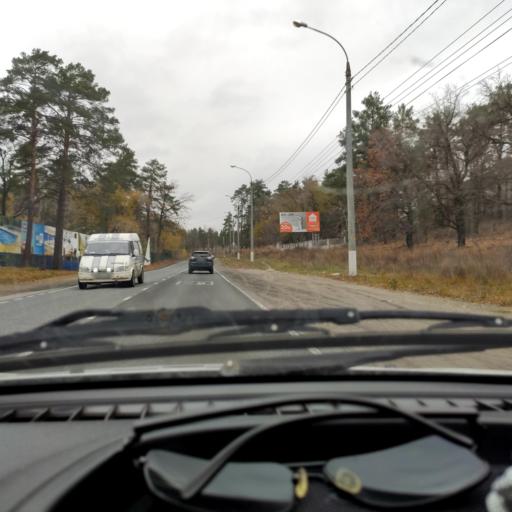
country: RU
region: Samara
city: Tol'yatti
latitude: 53.4843
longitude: 49.3165
